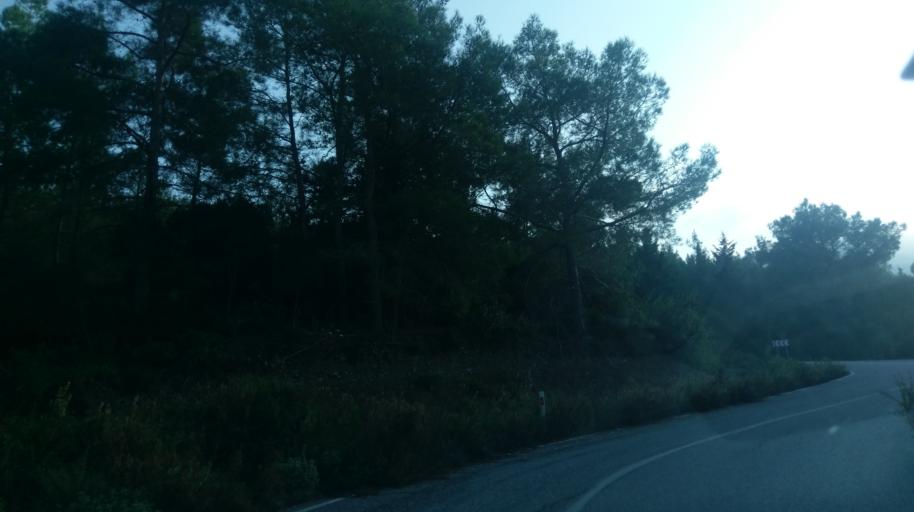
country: CY
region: Ammochostos
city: Trikomo
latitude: 35.3932
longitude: 33.8964
